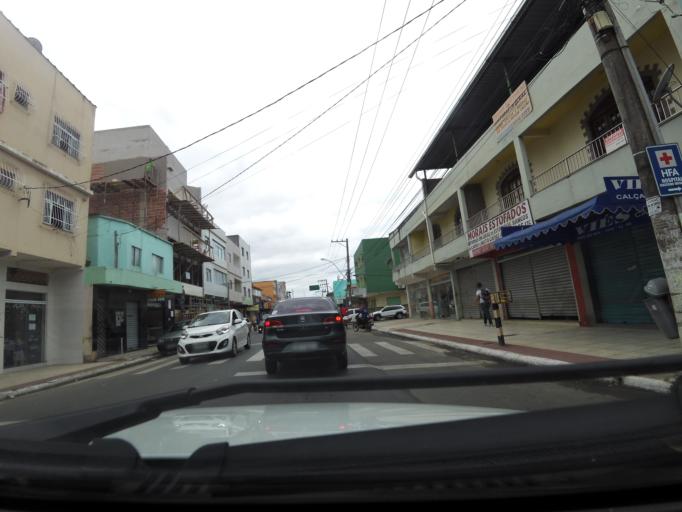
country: BR
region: Espirito Santo
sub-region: Guarapari
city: Guarapari
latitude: -20.6018
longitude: -40.4633
